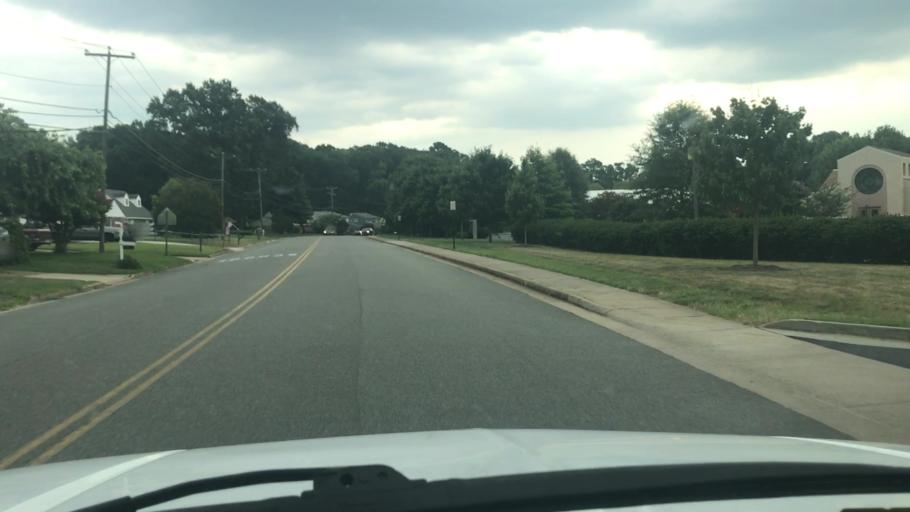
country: US
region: Virginia
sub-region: Henrico County
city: Tuckahoe
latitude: 37.6026
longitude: -77.5879
